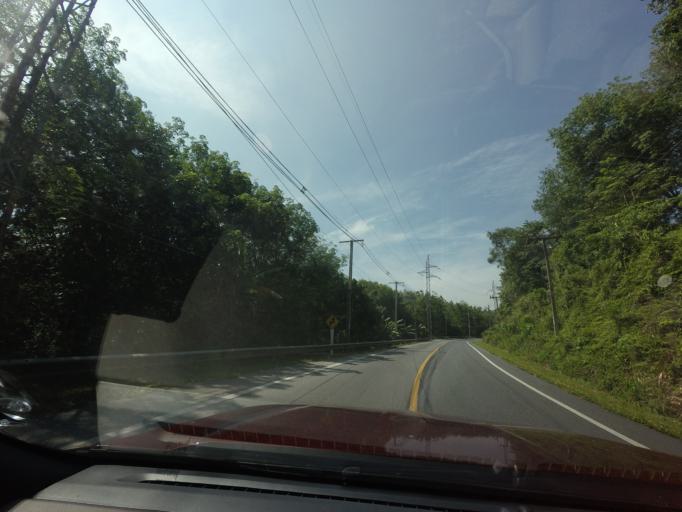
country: TH
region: Yala
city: Betong
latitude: 5.8394
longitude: 101.1188
